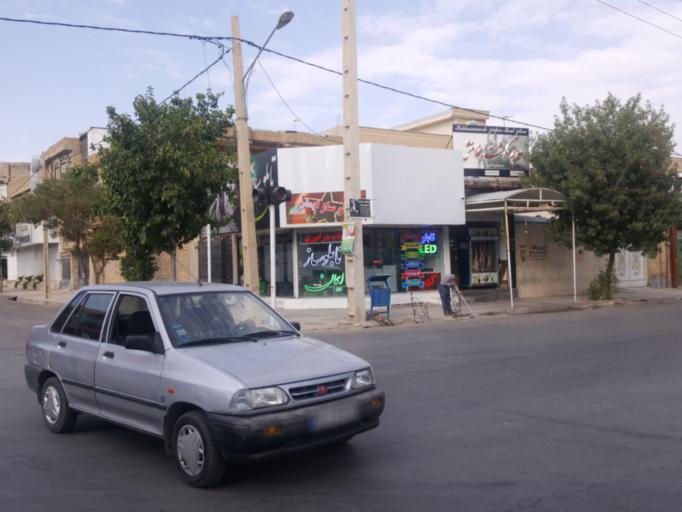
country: IR
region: Fars
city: Marvdasht
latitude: 29.8843
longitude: 52.8141
